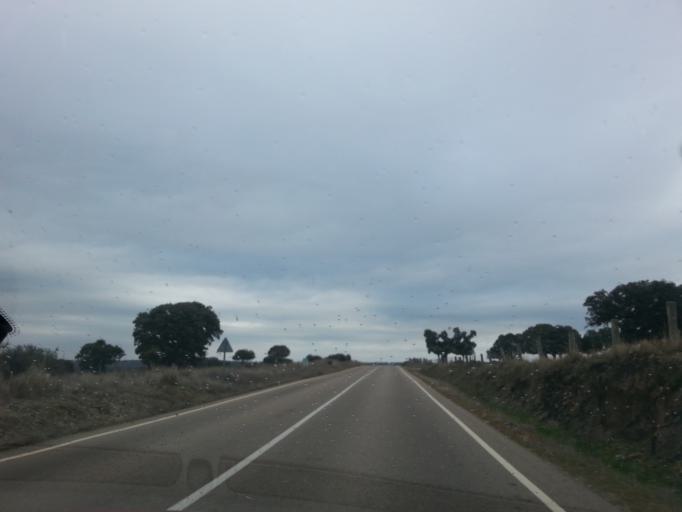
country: ES
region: Castille and Leon
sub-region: Provincia de Salamanca
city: Narros de Matalayegua
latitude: 40.7413
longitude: -5.9291
